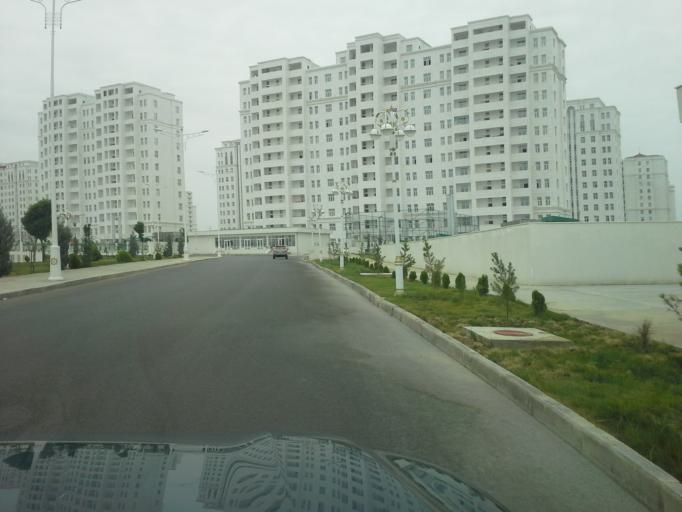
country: TM
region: Ahal
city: Ashgabat
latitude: 37.9188
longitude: 58.3678
